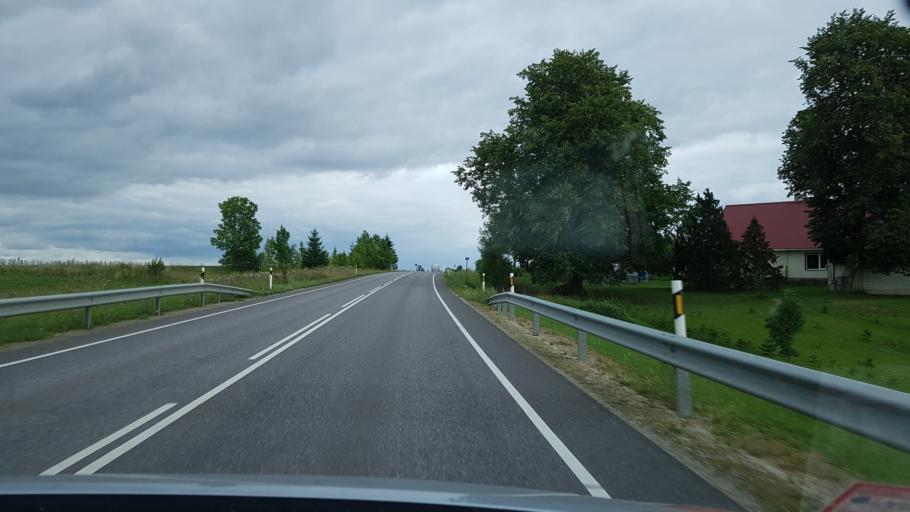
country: EE
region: Tartu
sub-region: Tartu linn
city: Tartu
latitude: 58.4301
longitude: 26.8460
